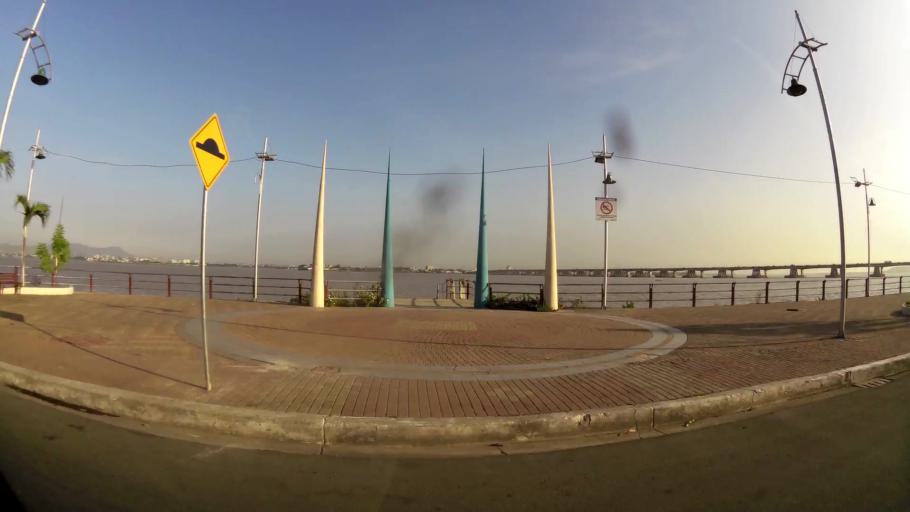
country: EC
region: Guayas
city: Eloy Alfaro
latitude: -2.1677
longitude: -79.8514
